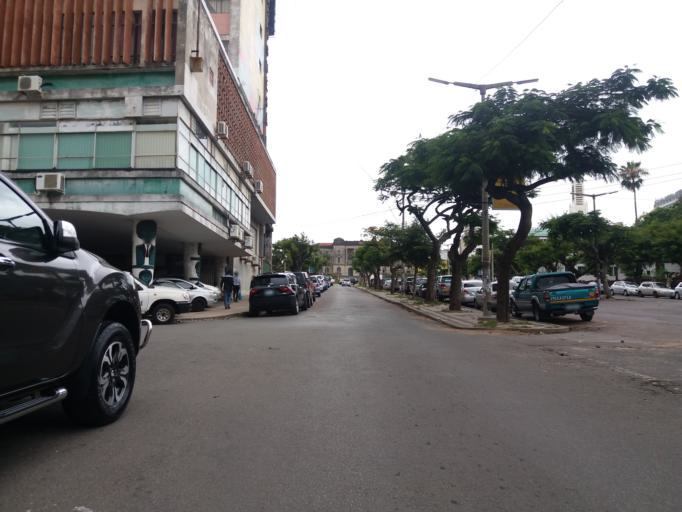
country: MZ
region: Maputo City
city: Maputo
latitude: -25.9707
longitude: 32.5722
